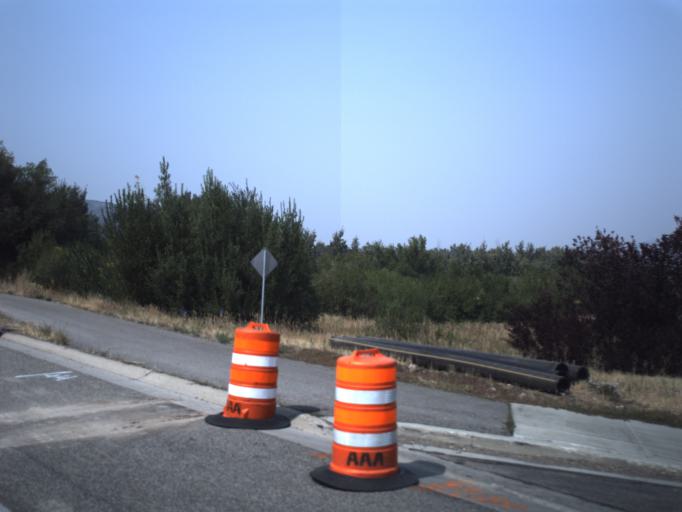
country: US
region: Utah
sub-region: Summit County
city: Snyderville
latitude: 40.6836
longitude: -111.5372
